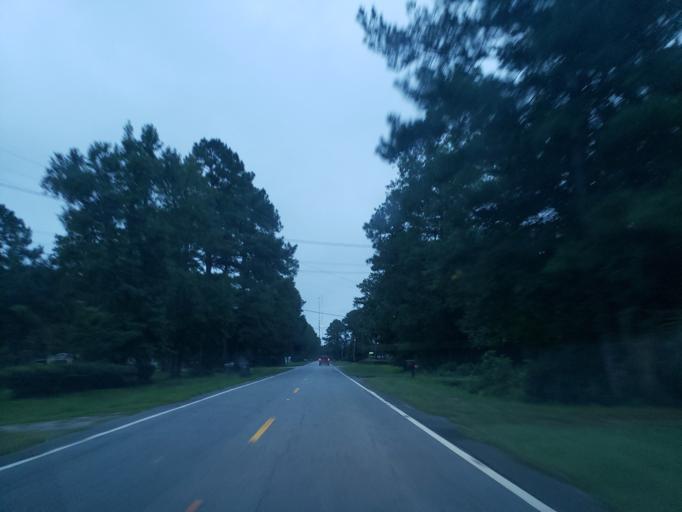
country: US
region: Georgia
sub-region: Chatham County
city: Bloomingdale
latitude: 32.0941
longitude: -81.3324
